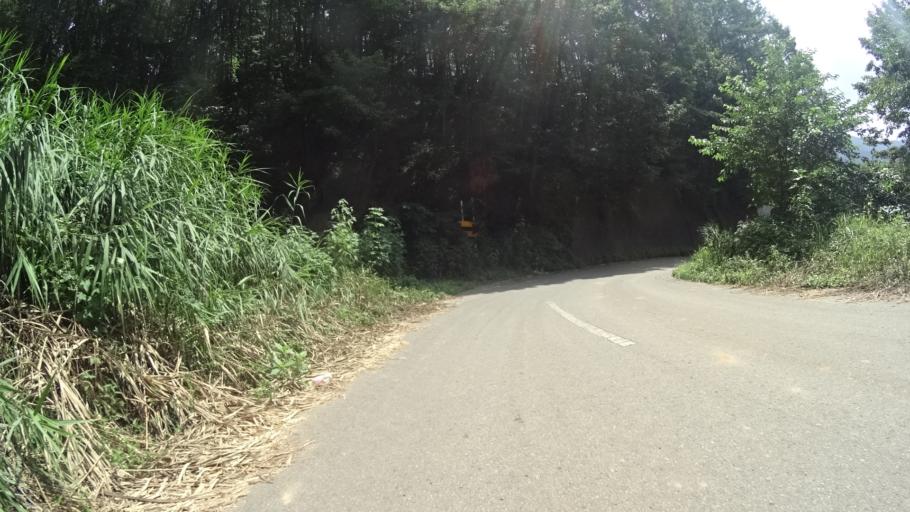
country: JP
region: Yamanashi
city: Nirasaki
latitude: 35.9053
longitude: 138.4681
